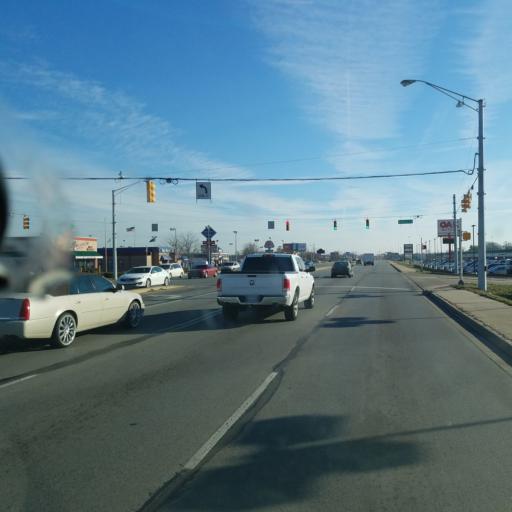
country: US
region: Indiana
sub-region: Marion County
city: Speedway
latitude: 39.8238
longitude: -86.2467
